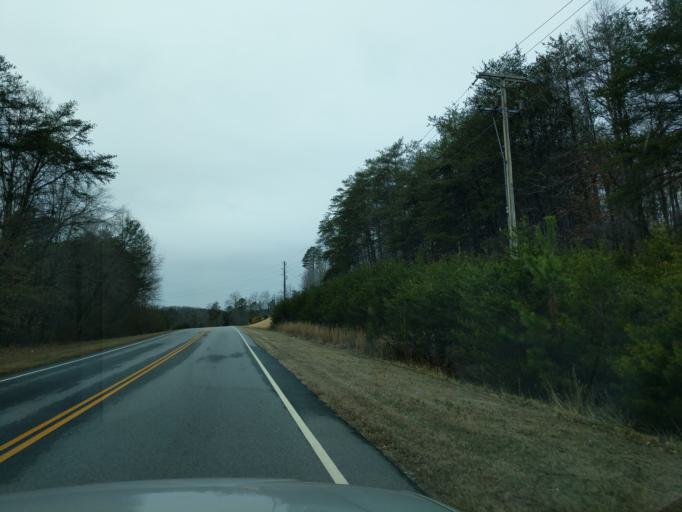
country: US
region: South Carolina
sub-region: Greenville County
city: Slater-Marietta
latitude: 35.0848
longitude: -82.4702
